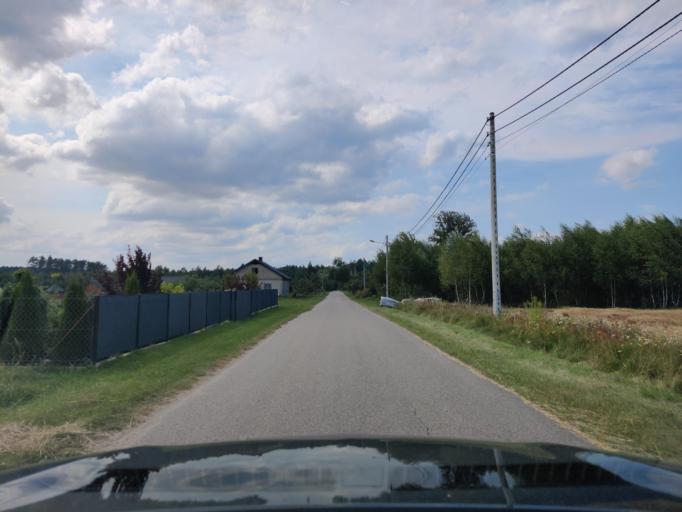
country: PL
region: Masovian Voivodeship
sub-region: Powiat pultuski
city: Obryte
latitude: 52.6903
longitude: 21.1773
